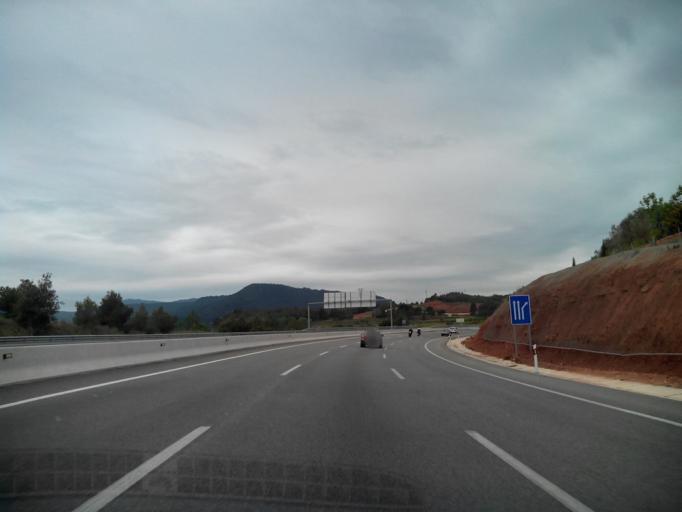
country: ES
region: Catalonia
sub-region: Provincia de Barcelona
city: Sant Joan de Vilatorrada
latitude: 41.7289
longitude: 1.7940
